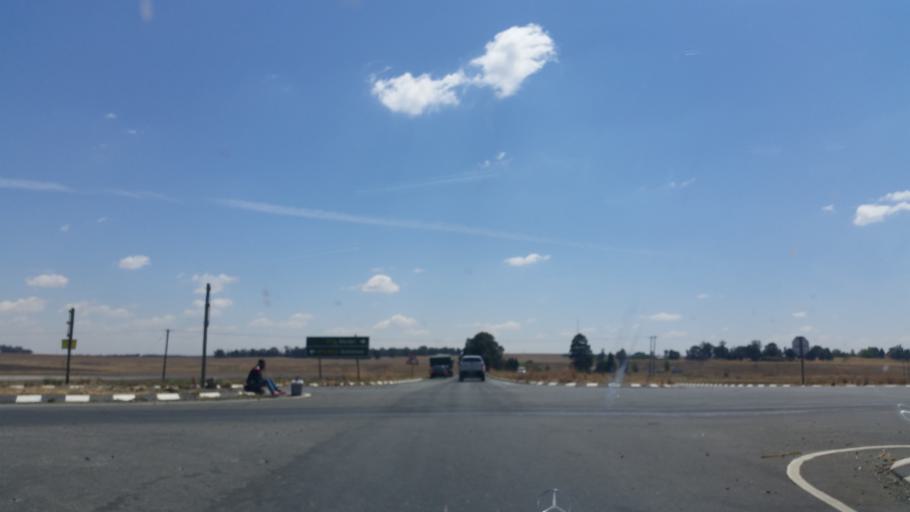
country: ZA
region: Orange Free State
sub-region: Thabo Mofutsanyana District Municipality
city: Reitz
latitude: -28.0834
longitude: 28.6494
